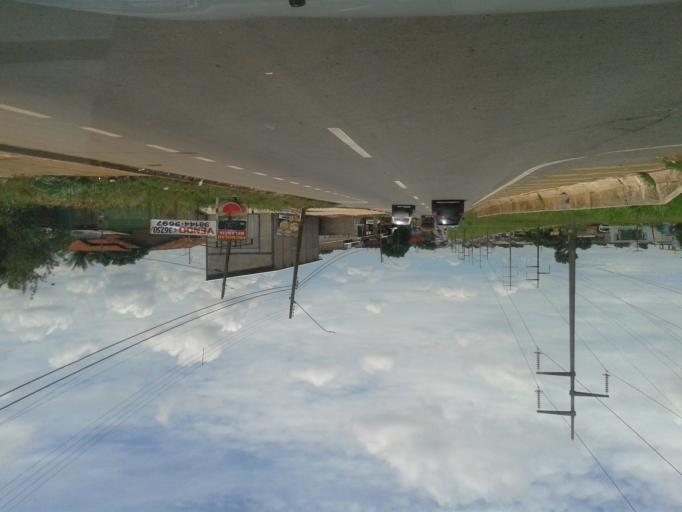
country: BR
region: Goias
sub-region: Aparecida De Goiania
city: Aparecida de Goiania
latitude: -16.7807
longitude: -49.2831
